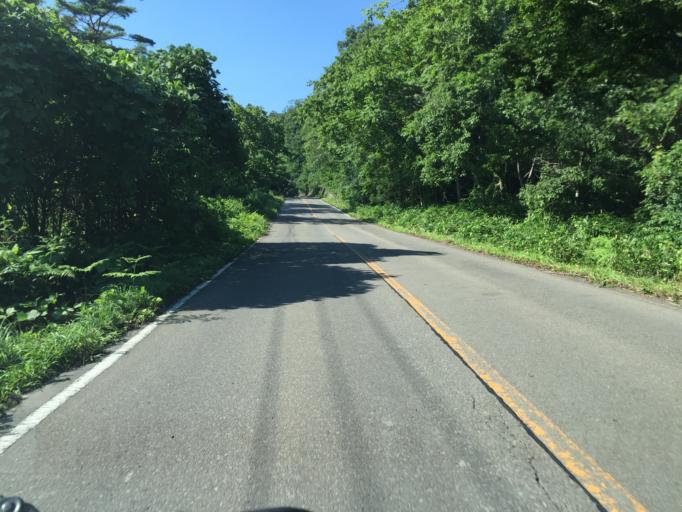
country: JP
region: Fukushima
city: Fukushima-shi
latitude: 37.8526
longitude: 140.4373
